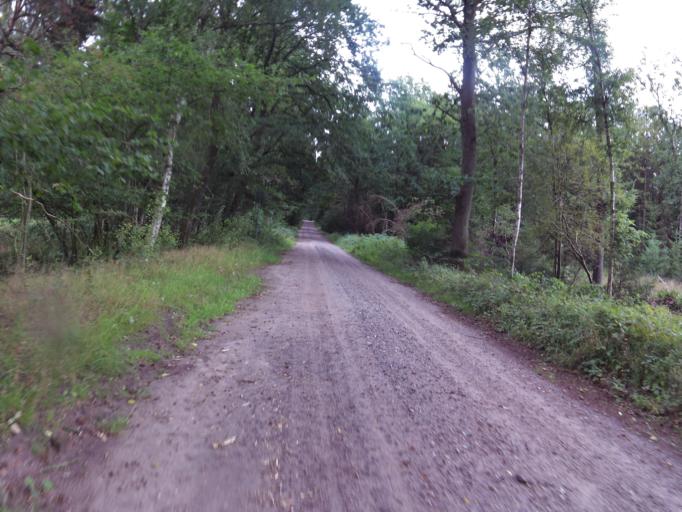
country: DE
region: Lower Saxony
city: Hipstedt
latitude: 53.5012
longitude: 8.9648
